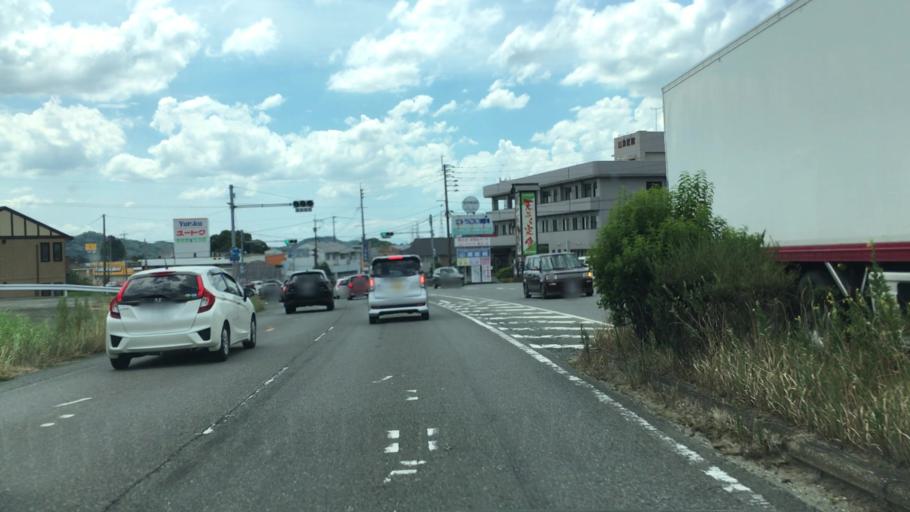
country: JP
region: Saga Prefecture
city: Tosu
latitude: 33.3908
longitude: 130.5010
